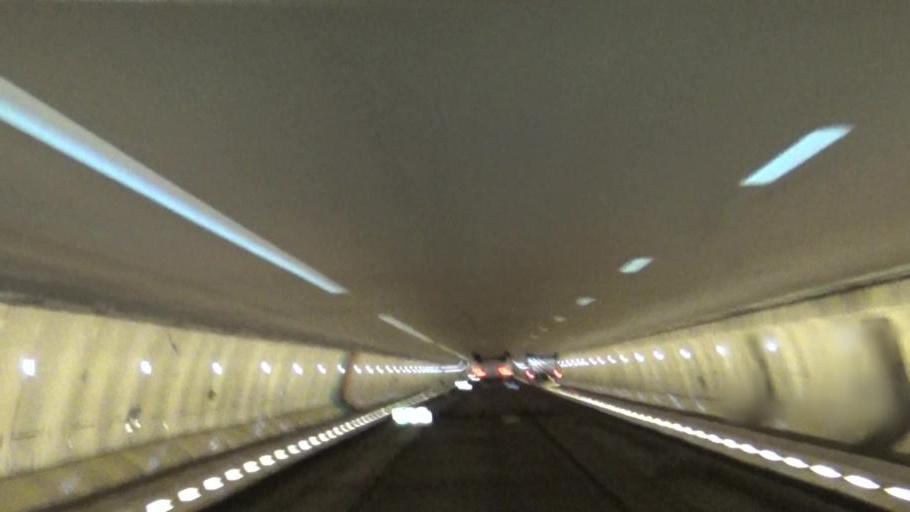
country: FR
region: Ile-de-France
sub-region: Departement des Yvelines
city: La Celle-Saint-Cloud
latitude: 48.8599
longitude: 2.1584
